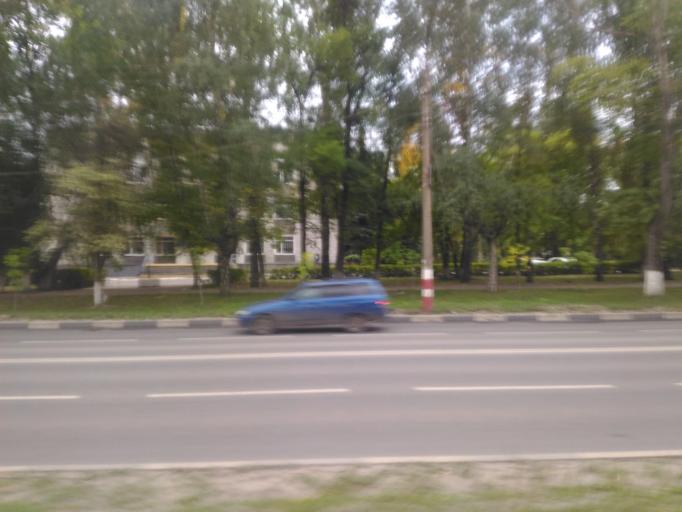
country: RU
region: Ulyanovsk
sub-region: Ulyanovskiy Rayon
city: Ulyanovsk
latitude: 54.2722
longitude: 48.3281
